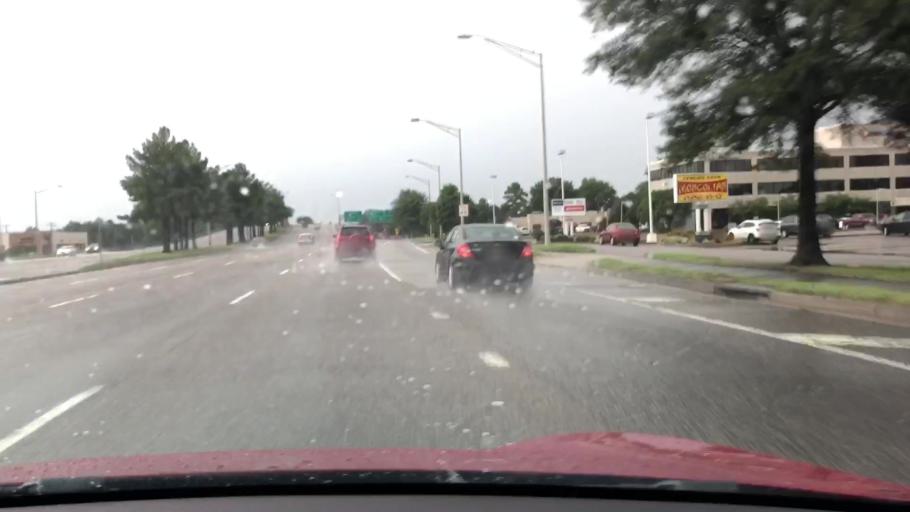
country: US
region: Virginia
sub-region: City of Chesapeake
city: Chesapeake
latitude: 36.8524
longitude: -76.2098
